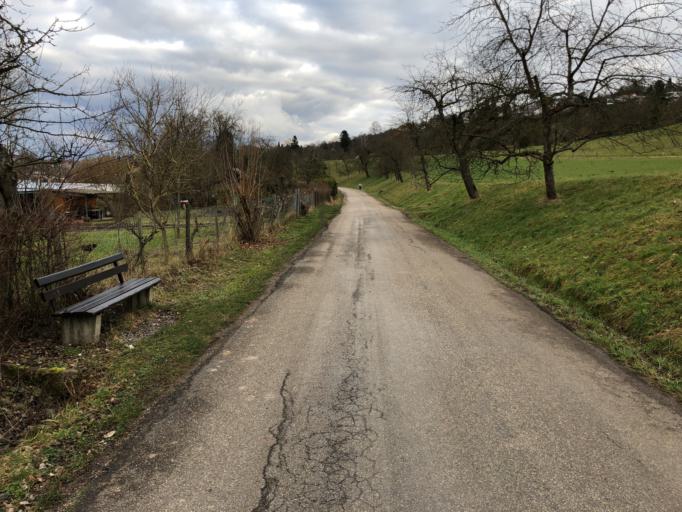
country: DE
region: Baden-Wuerttemberg
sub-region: Tuebingen Region
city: Tuebingen
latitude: 48.5180
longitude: 9.0277
